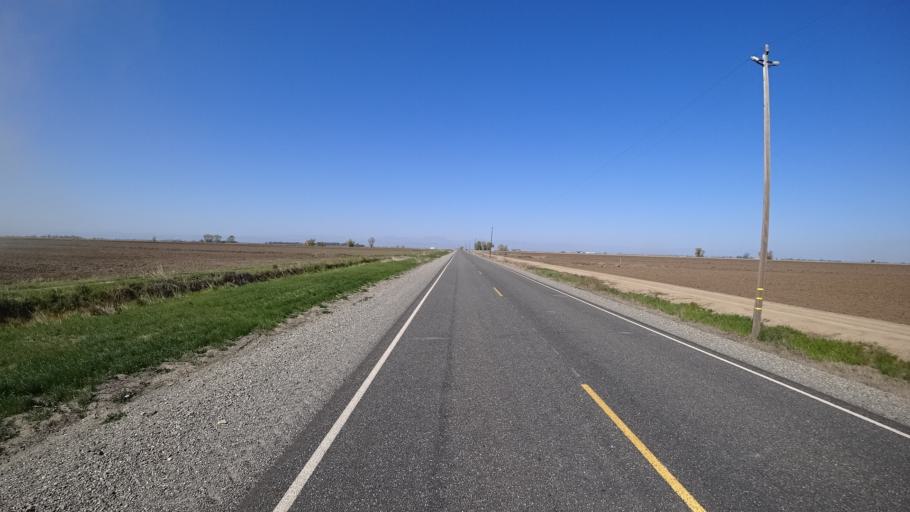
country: US
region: California
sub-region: Glenn County
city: Willows
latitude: 39.4579
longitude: -122.0793
